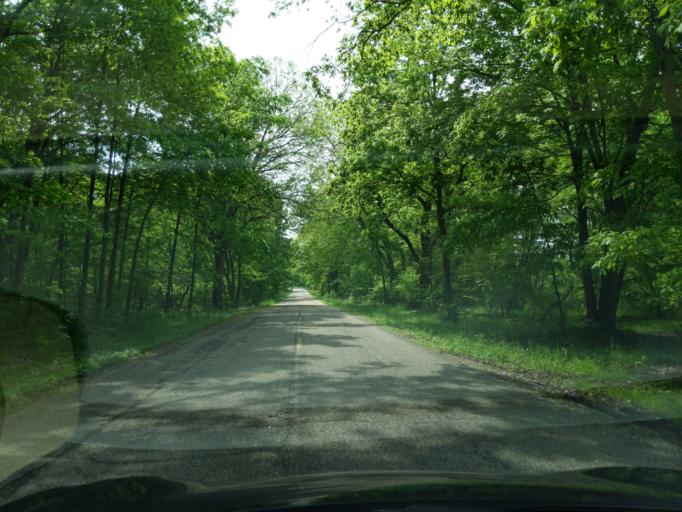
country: US
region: Michigan
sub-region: Ingham County
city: Leslie
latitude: 42.4319
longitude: -84.3519
